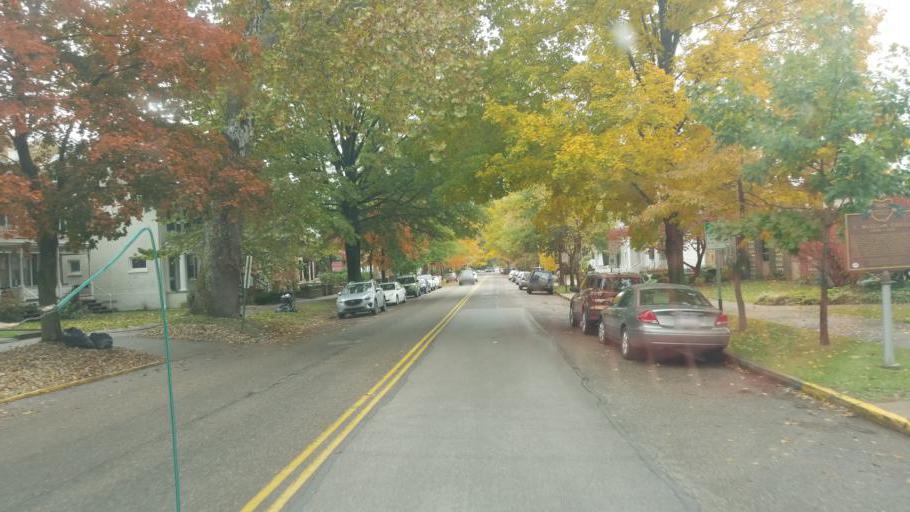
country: US
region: Ohio
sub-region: Washington County
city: Marietta
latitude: 39.4189
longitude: -81.4539
